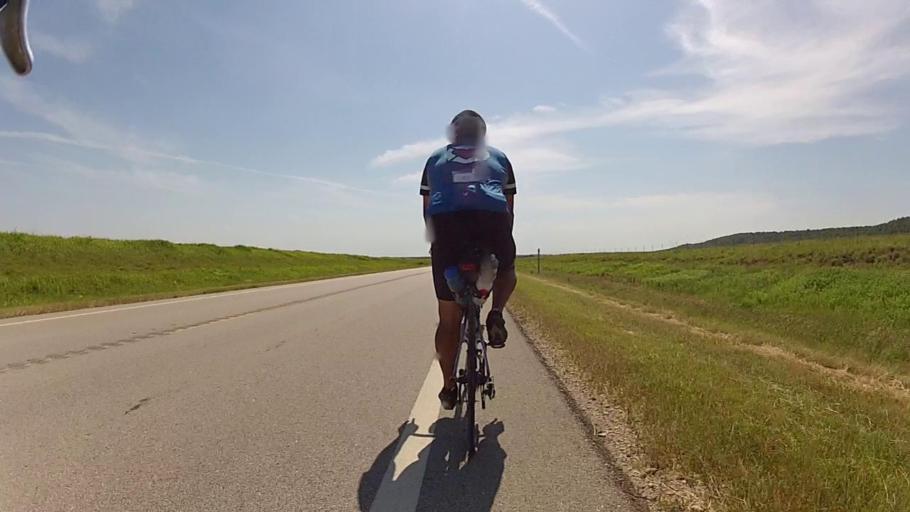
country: US
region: Kansas
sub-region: Chautauqua County
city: Sedan
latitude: 37.1067
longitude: -96.5540
